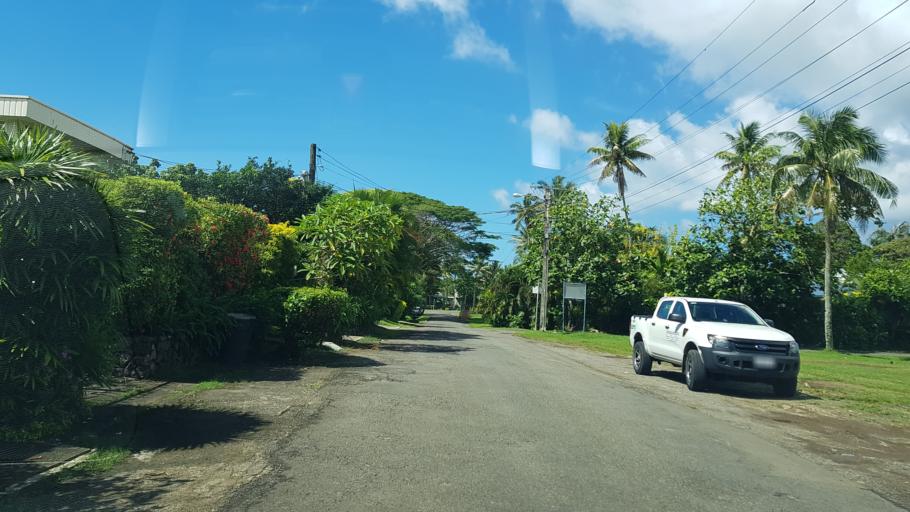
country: FJ
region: Central
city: Suva
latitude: -18.1478
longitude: 178.4550
